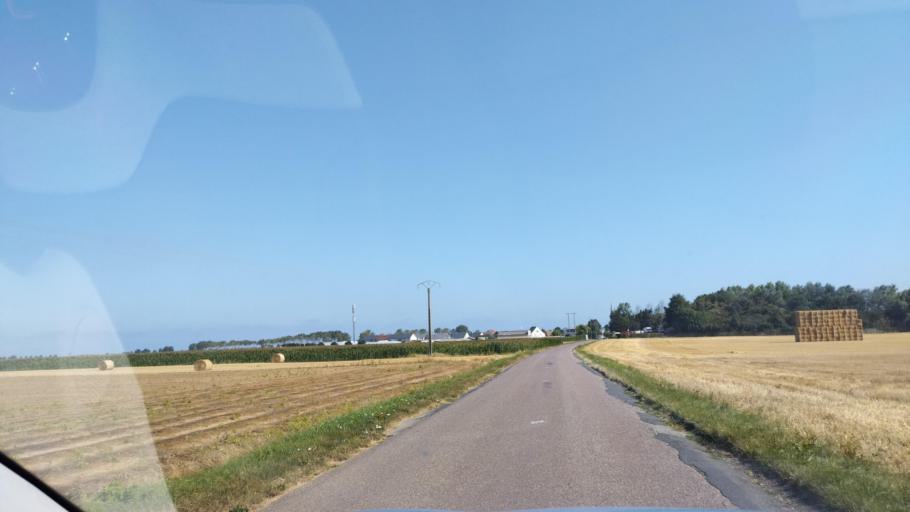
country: FR
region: Lower Normandy
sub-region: Departement du Calvados
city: Saint-Aubin-sur-Mer
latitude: 49.3195
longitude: -0.4010
